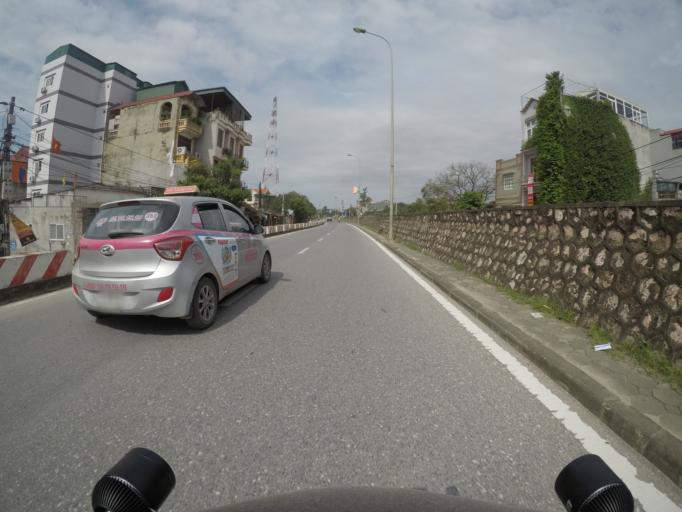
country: VN
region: Ha Noi
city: Tay Ho
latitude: 21.0932
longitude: 105.7796
